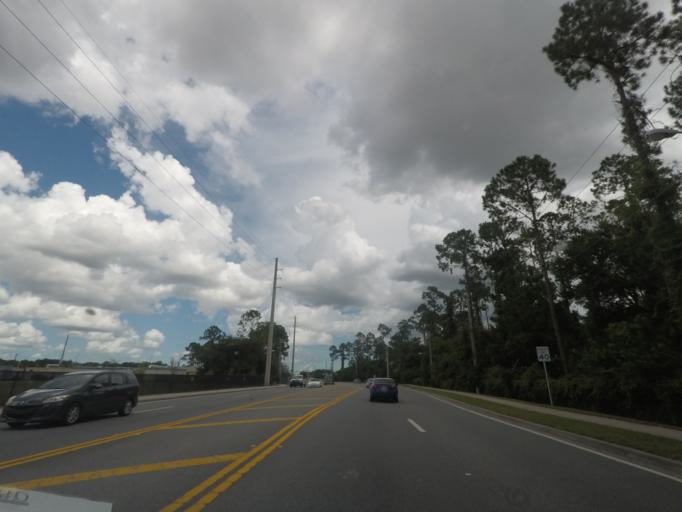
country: US
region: Florida
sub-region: Osceola County
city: Kissimmee
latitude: 28.3261
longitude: -81.4188
